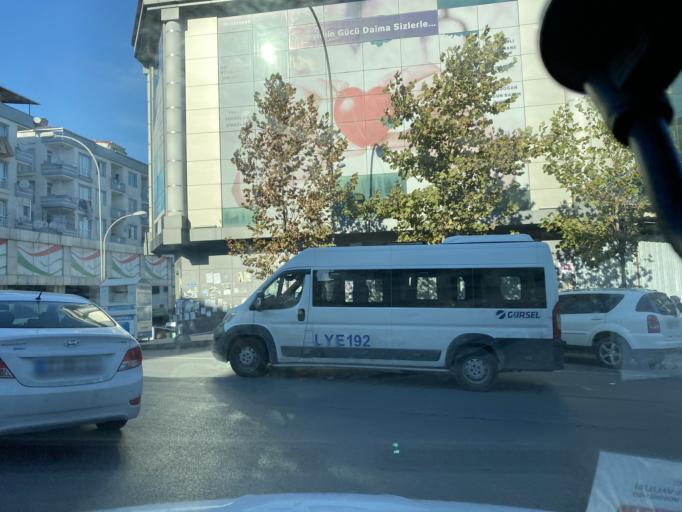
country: TR
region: Istanbul
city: Esenyurt
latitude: 41.0396
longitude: 28.6519
